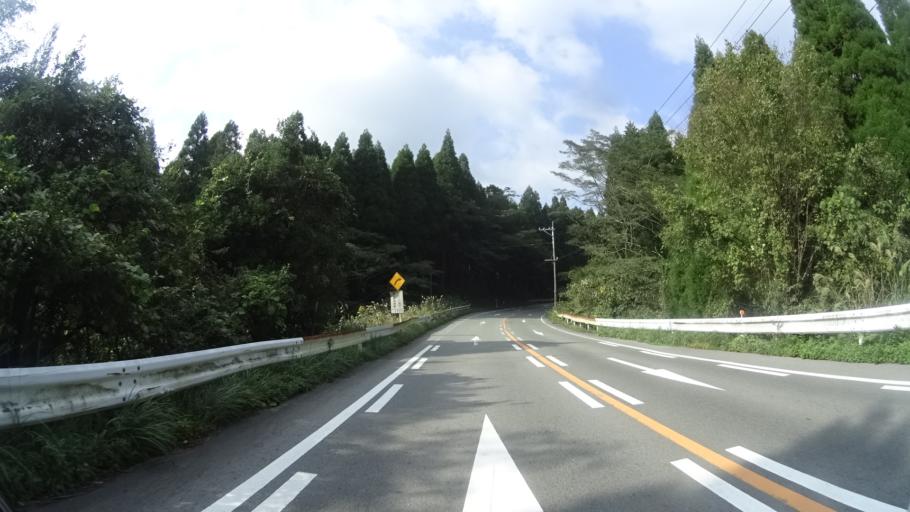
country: JP
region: Kumamoto
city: Aso
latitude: 33.0521
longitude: 131.0673
